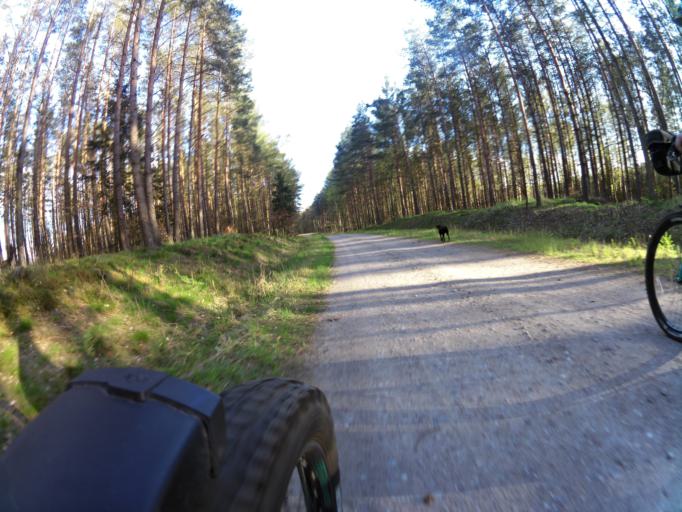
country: PL
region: West Pomeranian Voivodeship
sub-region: Powiat gryficki
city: Ploty
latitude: 53.7465
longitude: 15.2587
